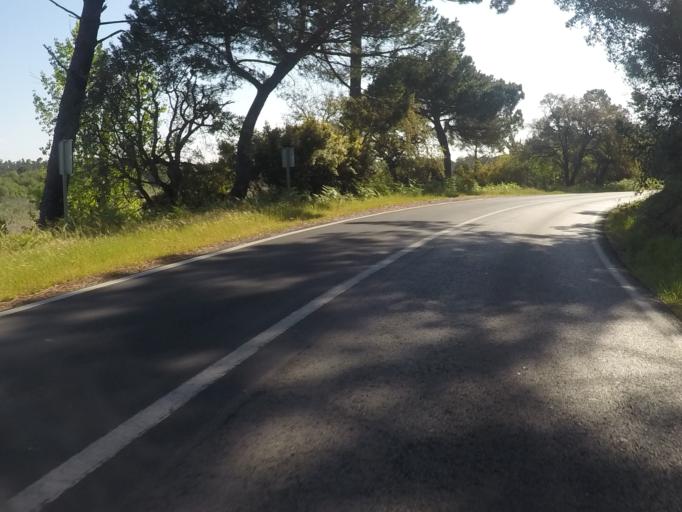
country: PT
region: Setubal
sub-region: Sesimbra
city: Sesimbra
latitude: 38.5266
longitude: -9.1364
